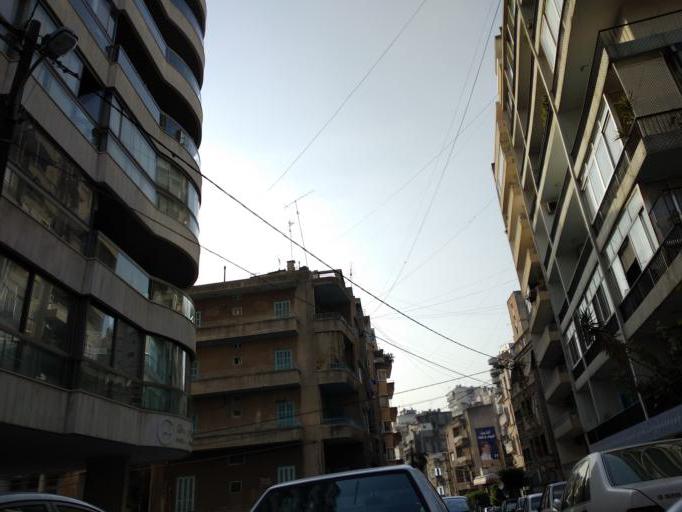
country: LB
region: Beyrouth
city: Beirut
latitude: 33.8874
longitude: 35.5261
